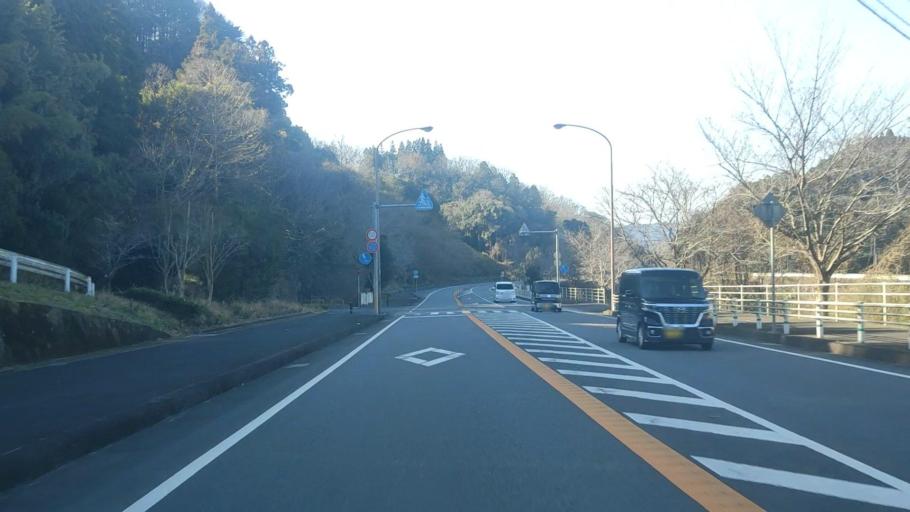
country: JP
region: Oita
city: Usuki
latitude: 33.0609
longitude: 131.6705
